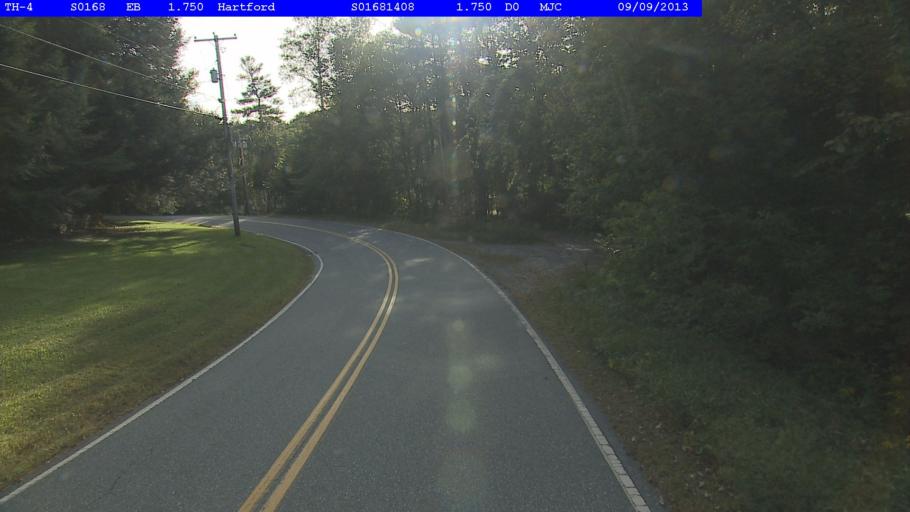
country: US
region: Vermont
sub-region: Windsor County
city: White River Junction
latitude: 43.6415
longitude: -72.4053
